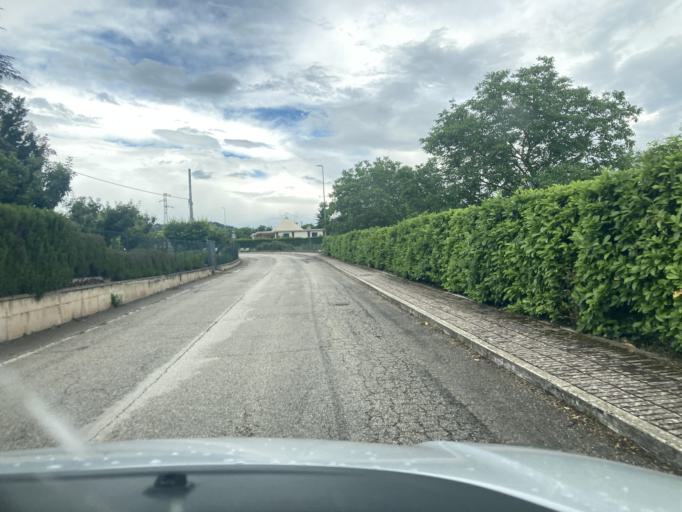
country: IT
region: Abruzzo
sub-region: Provincia dell' Aquila
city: San Demetrio Ne' Vestini
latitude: 42.2931
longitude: 13.5564
